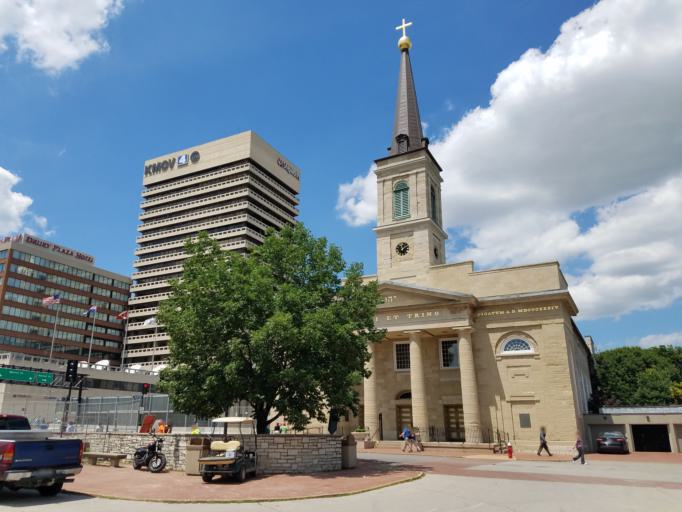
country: US
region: Missouri
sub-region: City of Saint Louis
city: St. Louis
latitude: 38.6234
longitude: -90.1873
